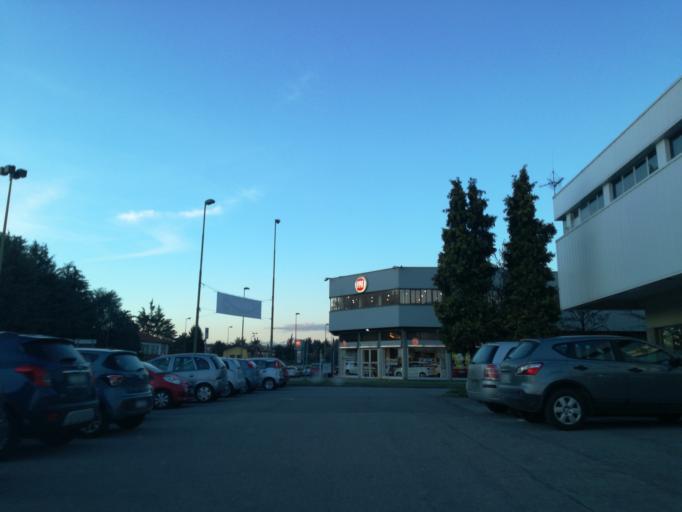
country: IT
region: Lombardy
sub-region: Provincia di Monza e Brianza
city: Vimercate
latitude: 45.6132
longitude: 9.3594
